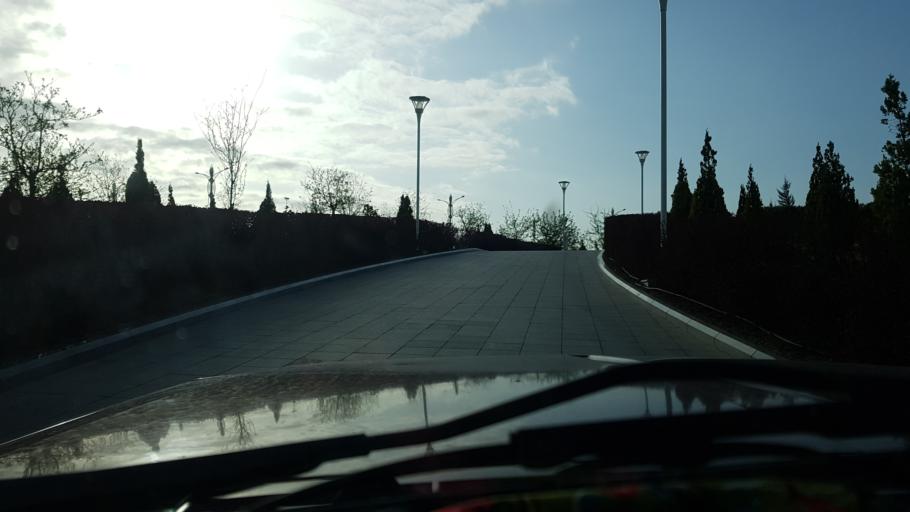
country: TM
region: Ahal
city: Ashgabat
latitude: 37.9286
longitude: 58.3330
